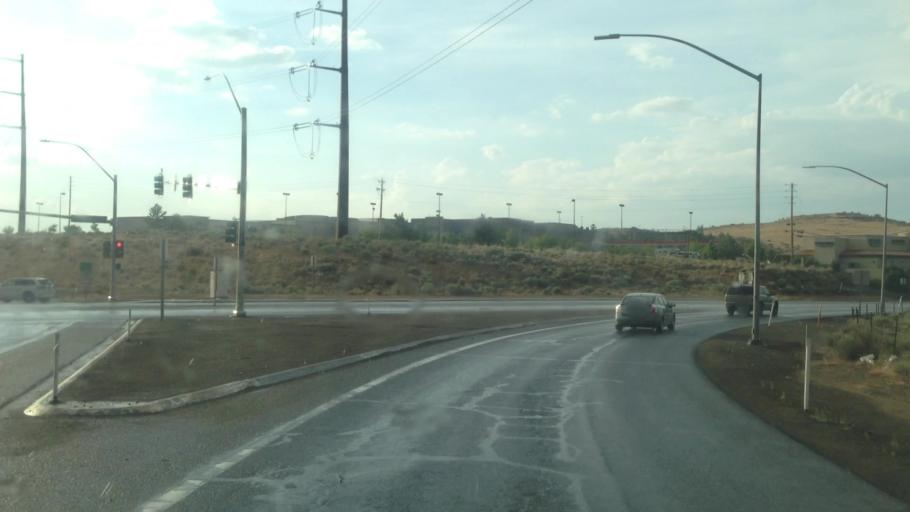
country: US
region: Nevada
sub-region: Washoe County
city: Golden Valley
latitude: 39.6114
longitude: -119.8500
